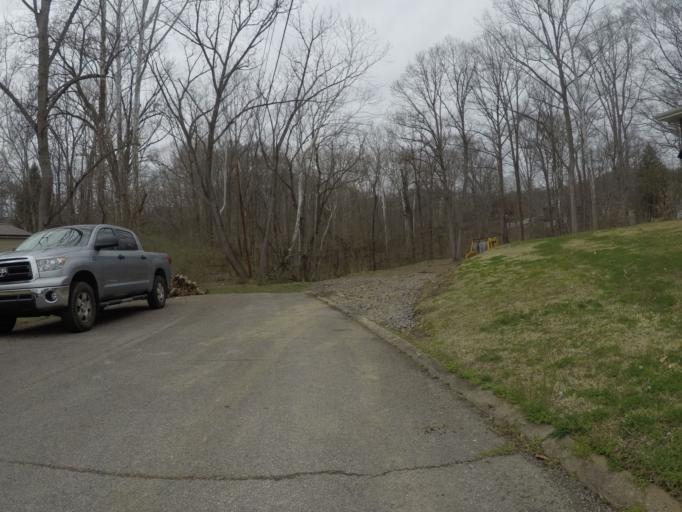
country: US
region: West Virginia
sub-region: Cabell County
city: Pea Ridge
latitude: 38.4213
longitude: -82.3246
